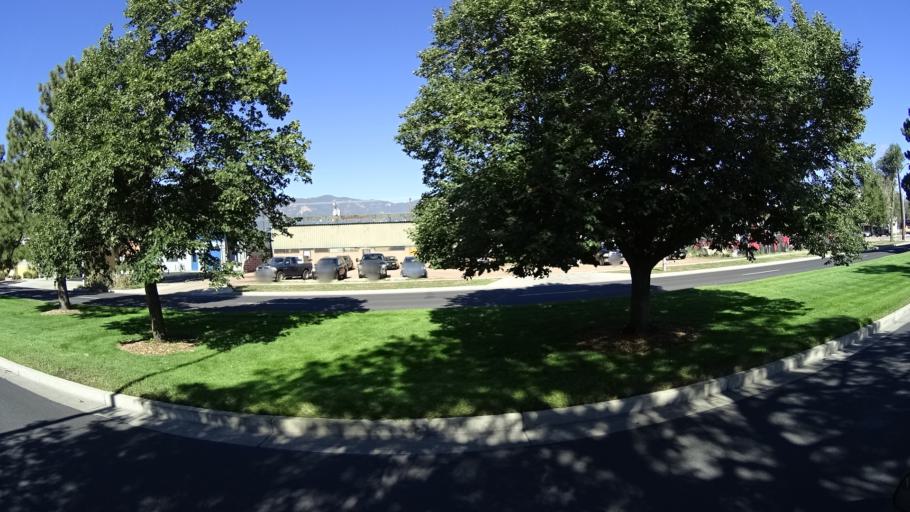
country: US
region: Colorado
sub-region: El Paso County
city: Colorado Springs
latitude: 38.8287
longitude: -104.8182
